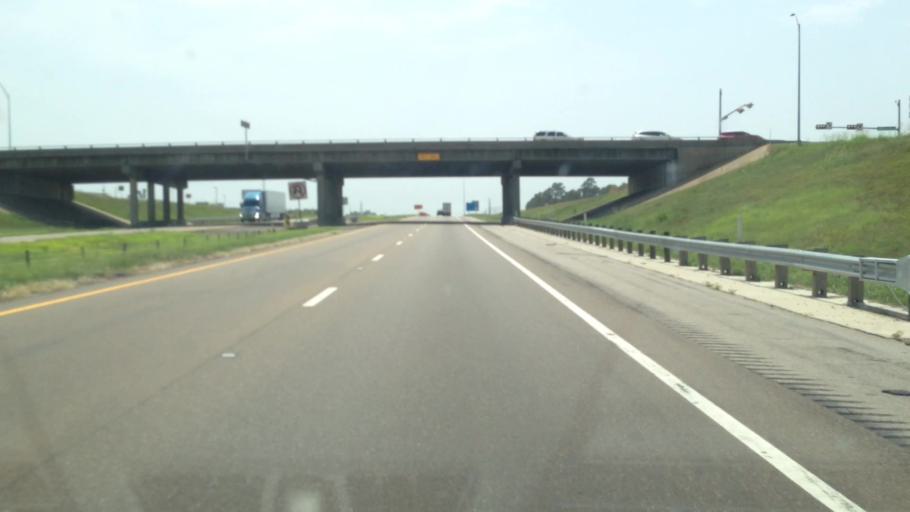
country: US
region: Texas
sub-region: Titus County
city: Mount Pleasant
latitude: 33.1792
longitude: -94.9697
